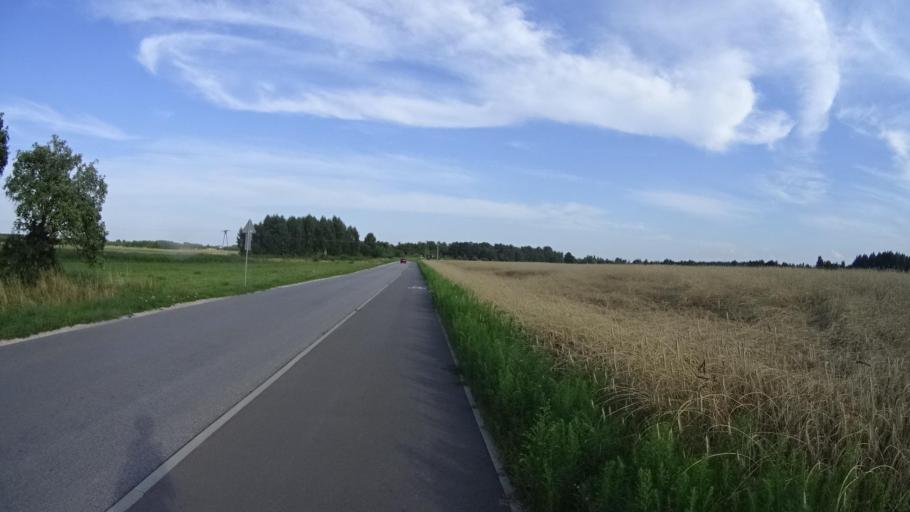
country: PL
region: Masovian Voivodeship
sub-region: Powiat piaseczynski
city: Tarczyn
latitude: 52.0151
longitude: 20.7981
